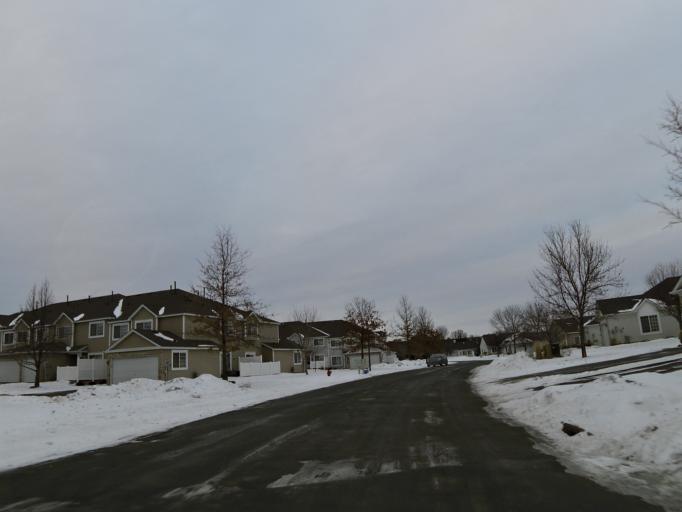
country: US
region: Minnesota
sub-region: Washington County
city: Woodbury
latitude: 44.9389
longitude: -92.9015
